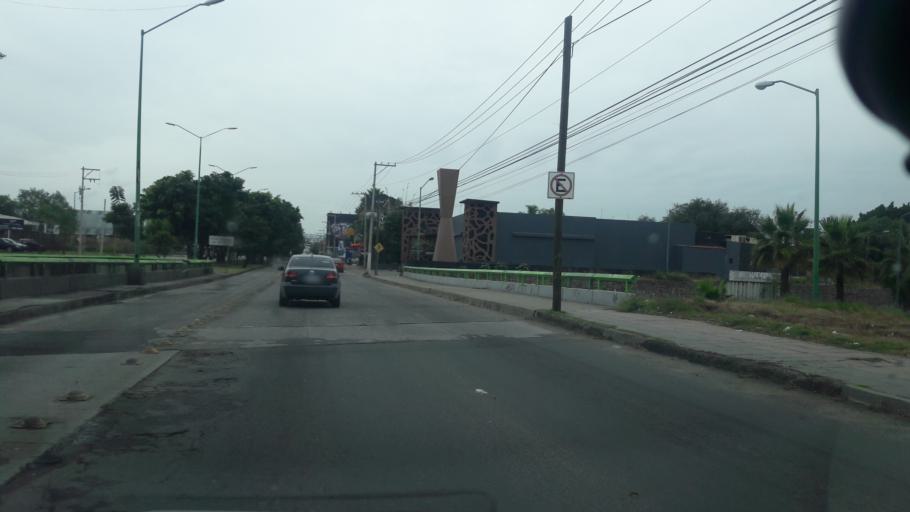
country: MX
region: Guanajuato
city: Leon
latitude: 21.1478
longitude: -101.6778
